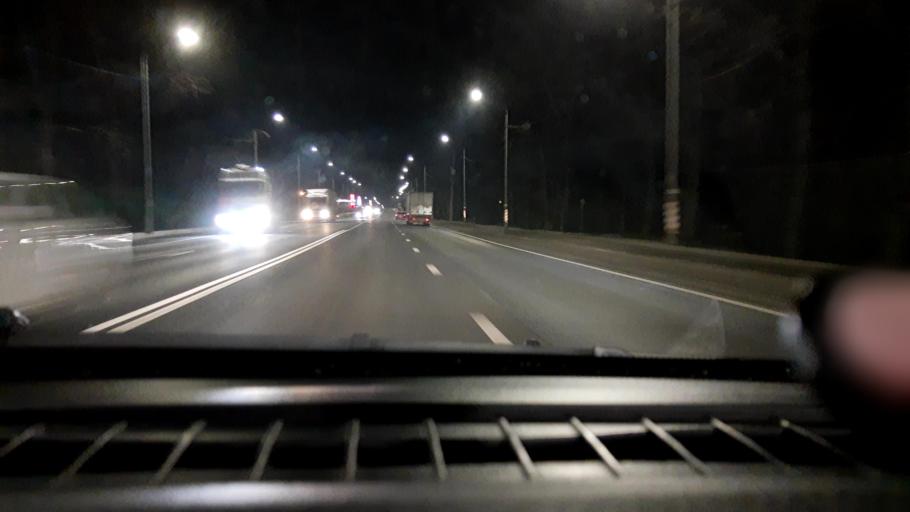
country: RU
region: Nizjnij Novgorod
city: Lyskovo
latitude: 56.0139
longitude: 45.0239
